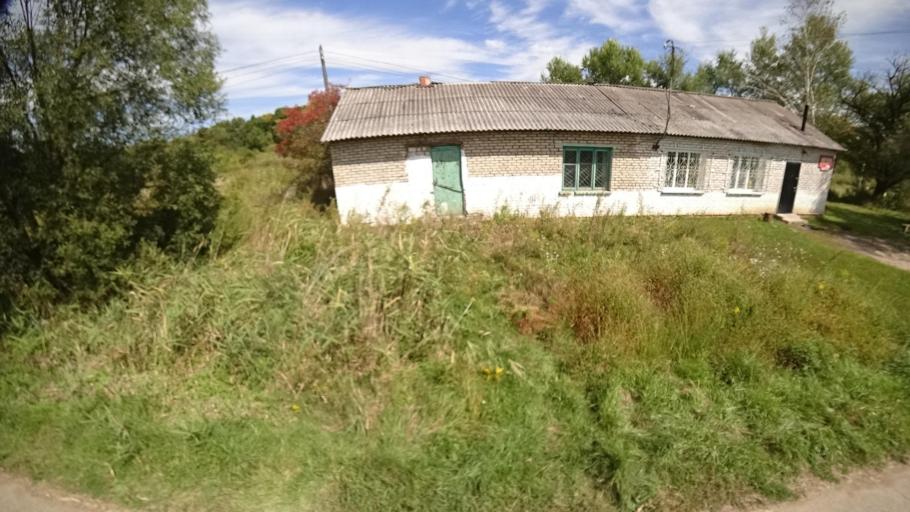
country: RU
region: Primorskiy
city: Yakovlevka
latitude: 44.6451
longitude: 133.5923
